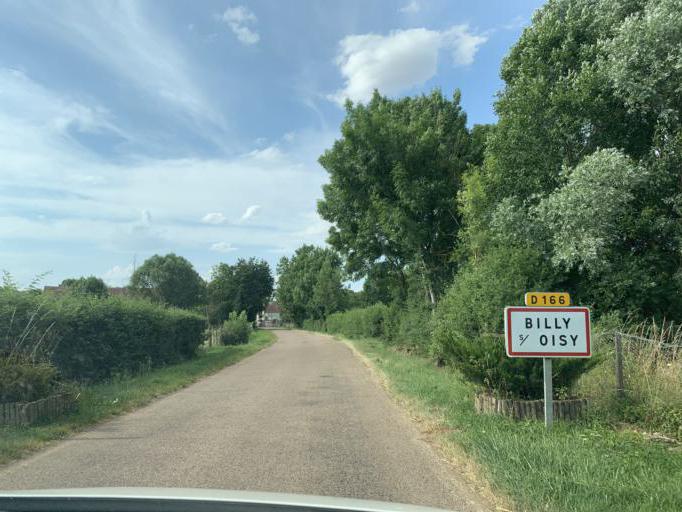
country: FR
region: Bourgogne
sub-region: Departement de l'Yonne
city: Fontenailles
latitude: 47.4787
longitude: 3.4218
